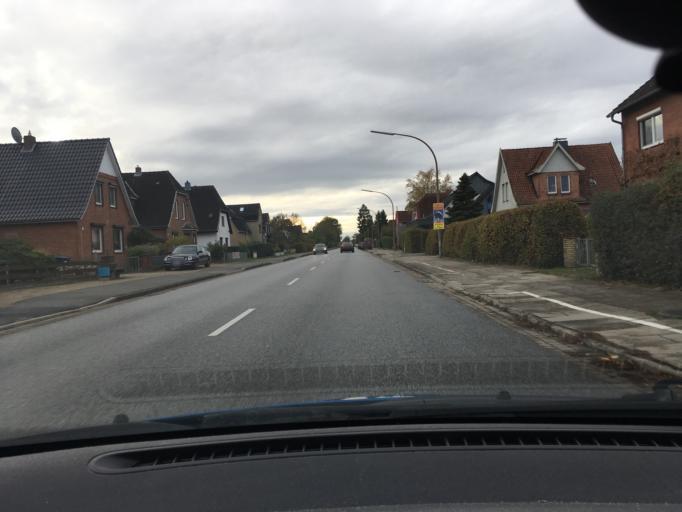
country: DE
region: Schleswig-Holstein
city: Schwarzenbek
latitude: 53.5010
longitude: 10.4682
